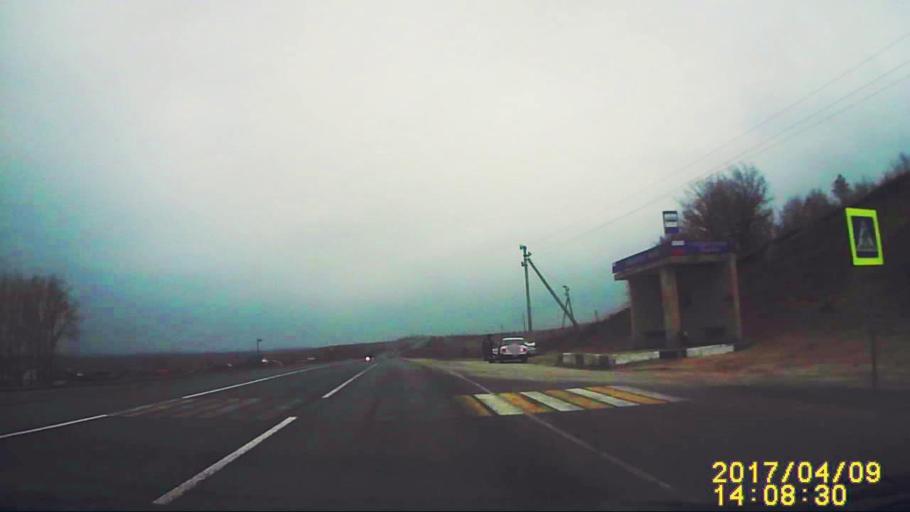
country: RU
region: Ulyanovsk
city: Silikatnyy
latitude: 54.0204
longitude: 48.2154
